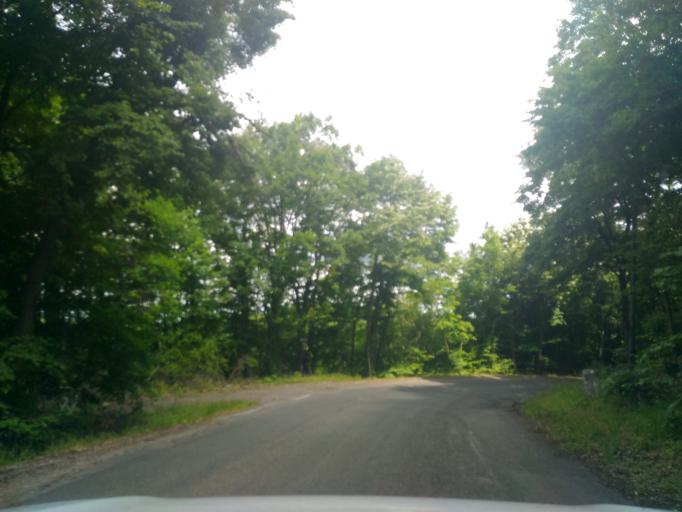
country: HU
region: Baranya
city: Pecs
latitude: 46.1333
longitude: 18.2318
